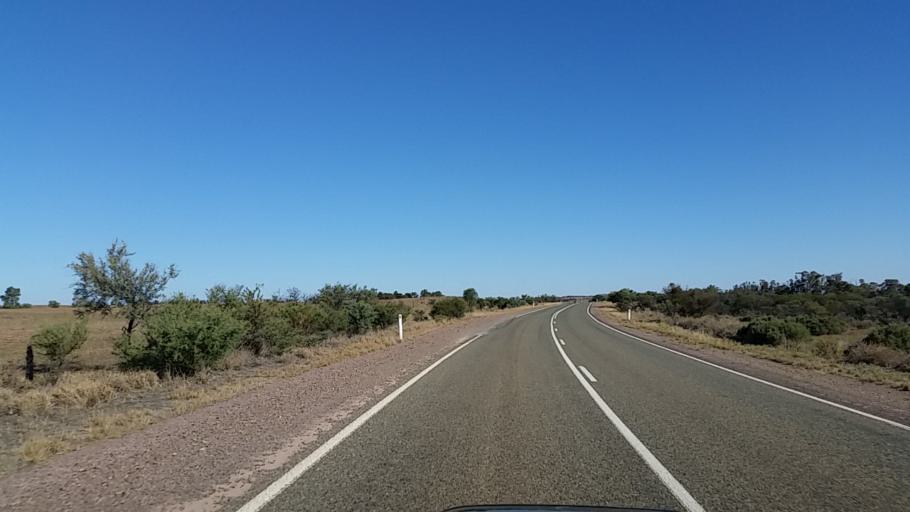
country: AU
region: South Australia
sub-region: Flinders Ranges
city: Quorn
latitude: -32.4588
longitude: 138.5378
